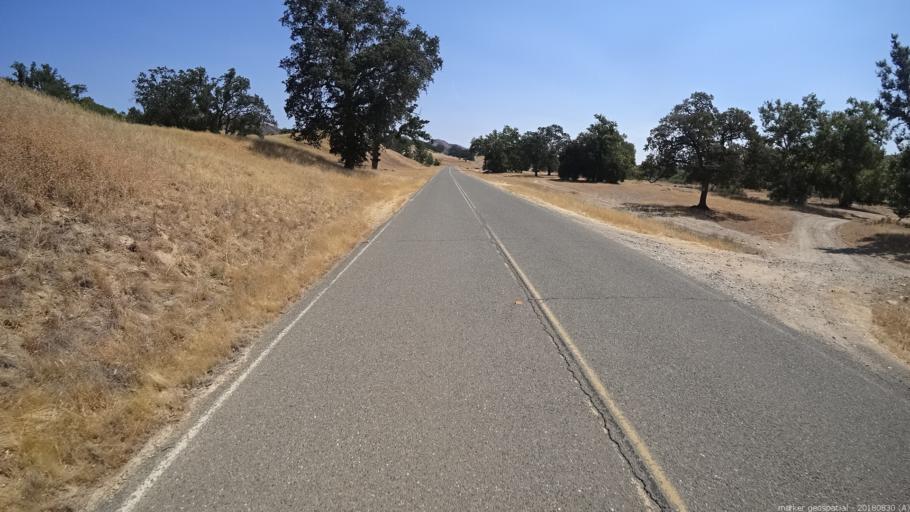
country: US
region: California
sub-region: Monterey County
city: King City
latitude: 35.9762
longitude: -121.3416
